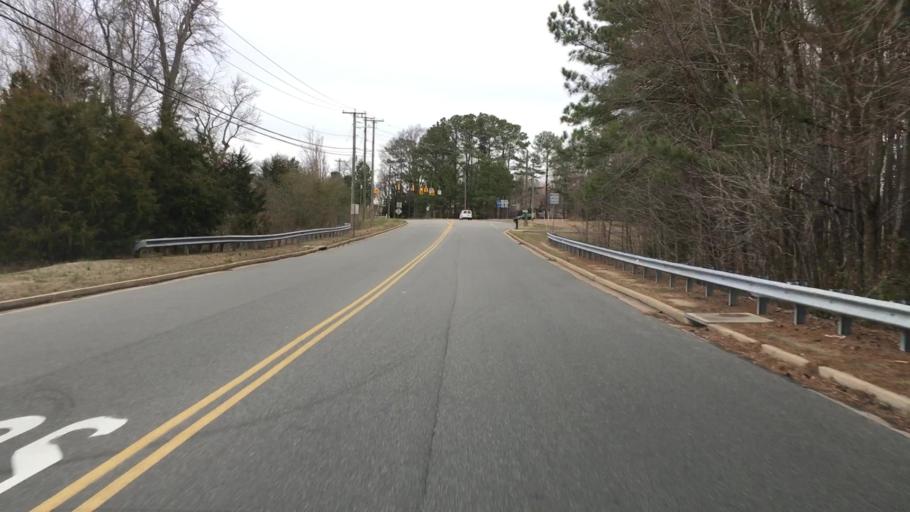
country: US
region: Virginia
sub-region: Henrico County
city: Glen Allen
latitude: 37.6698
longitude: -77.5421
